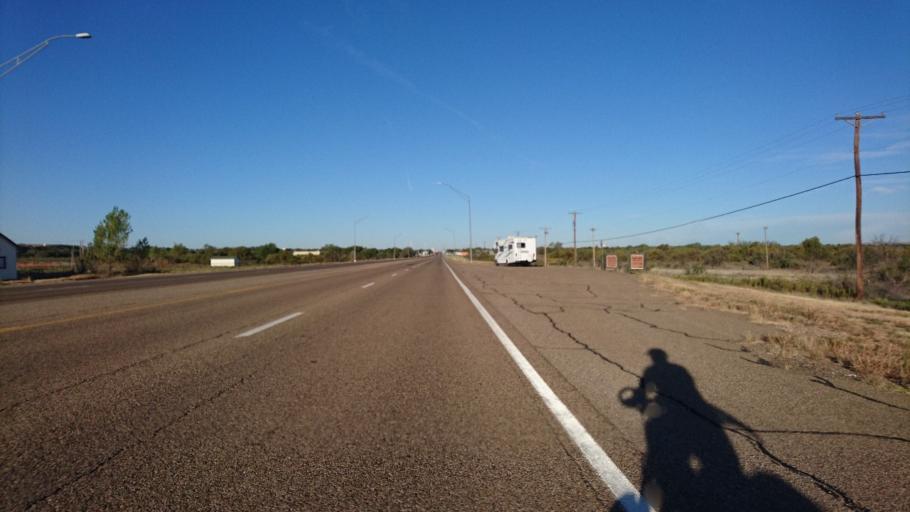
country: US
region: New Mexico
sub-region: Quay County
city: Tucumcari
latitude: 35.1720
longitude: -103.6932
